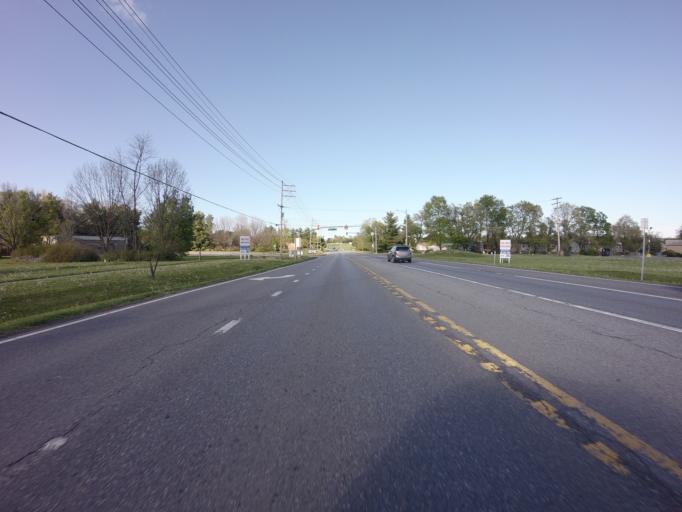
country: US
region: Maryland
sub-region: Frederick County
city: Walkersville
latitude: 39.4863
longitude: -77.3411
